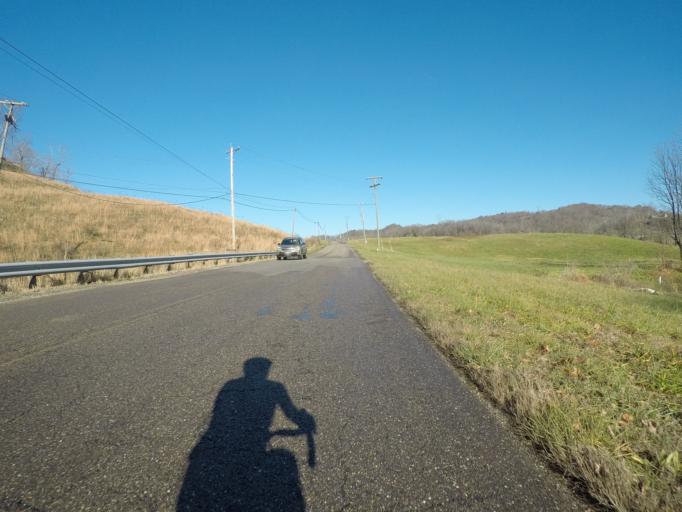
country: US
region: West Virginia
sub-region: Cabell County
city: Huntington
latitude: 38.4821
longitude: -82.4678
